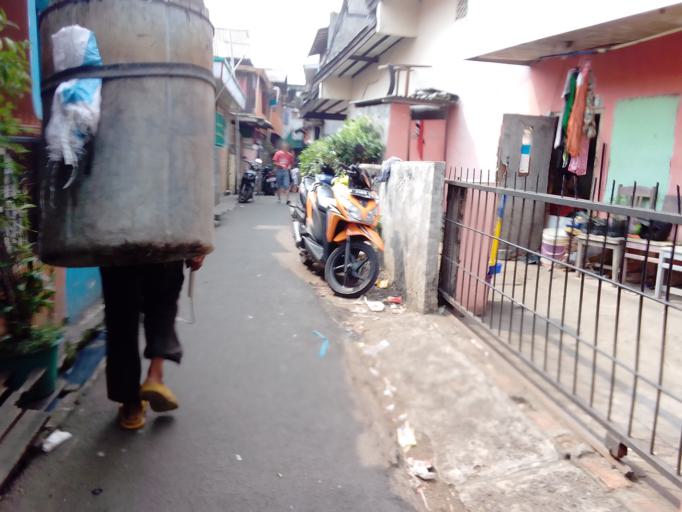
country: ID
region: Jakarta Raya
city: Jakarta
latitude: -6.1939
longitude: 106.8071
